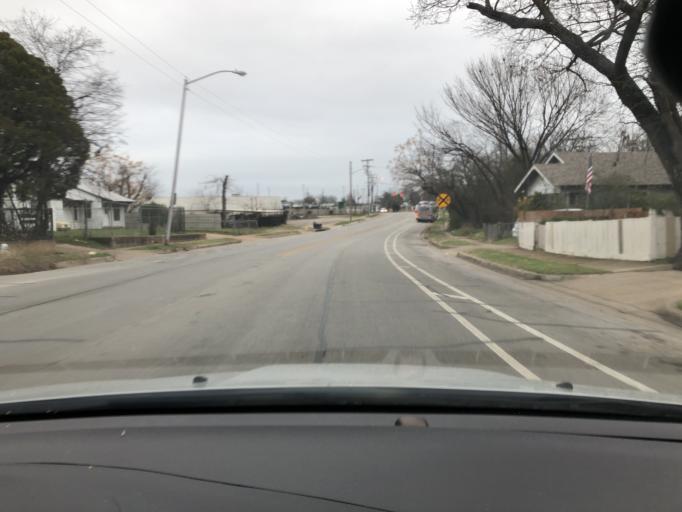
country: US
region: Texas
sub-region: Tarrant County
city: Fort Worth
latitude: 32.7271
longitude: -97.3053
